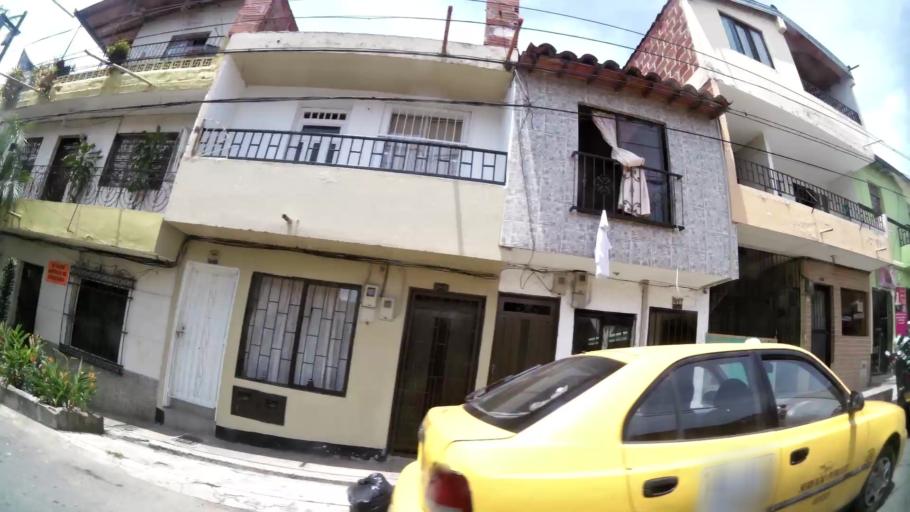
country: CO
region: Antioquia
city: Bello
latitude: 6.3492
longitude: -75.5669
